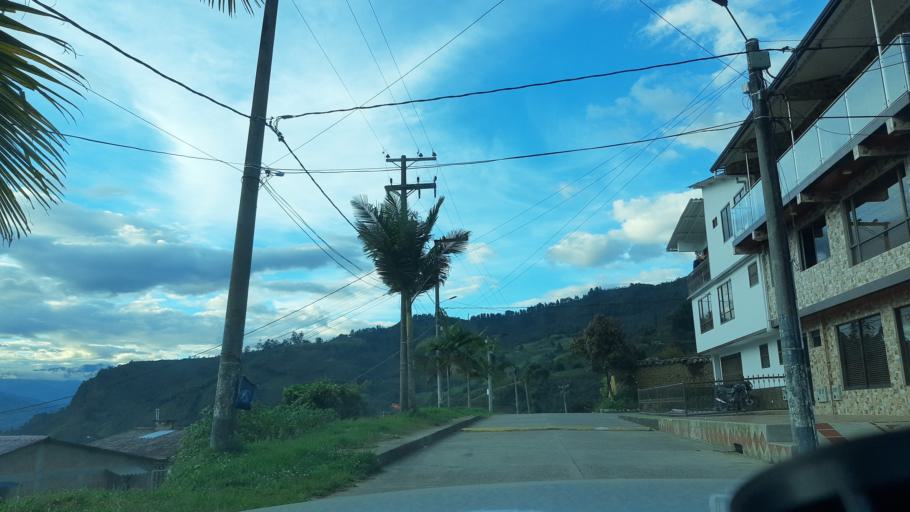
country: CO
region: Boyaca
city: Chivor
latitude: 4.9707
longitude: -73.3225
